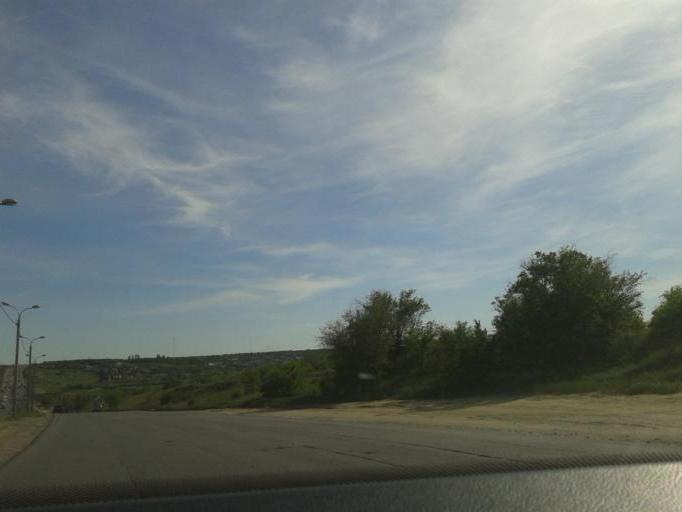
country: RU
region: Volgograd
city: Volgograd
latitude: 48.7246
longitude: 44.4468
